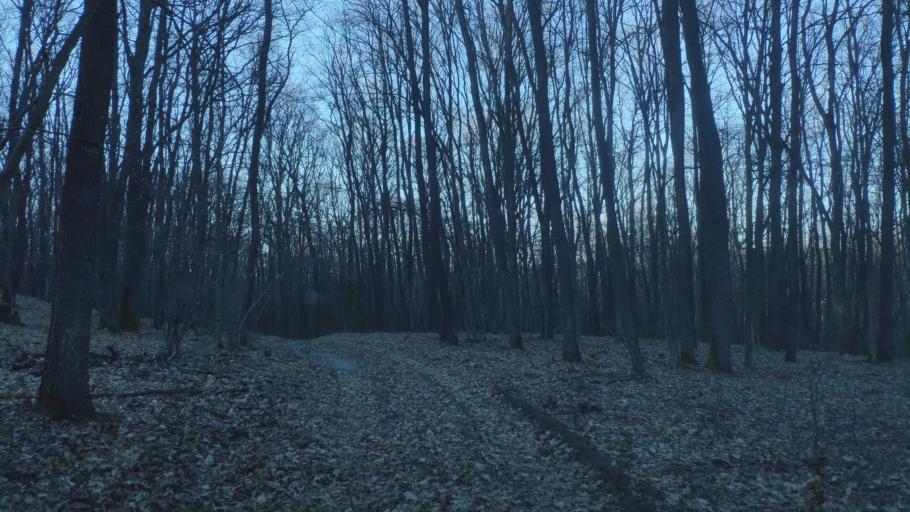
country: HU
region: Borsod-Abauj-Zemplen
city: Putnok
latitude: 48.5049
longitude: 20.3270
